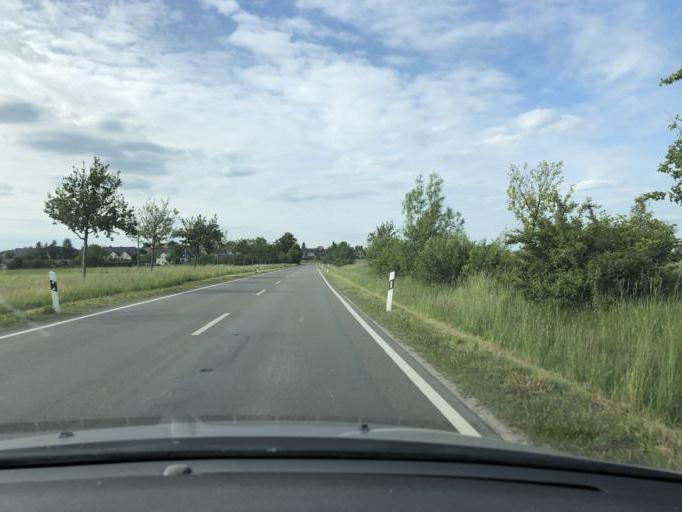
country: DE
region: Saxony
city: Brandis
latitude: 51.3131
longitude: 12.6471
